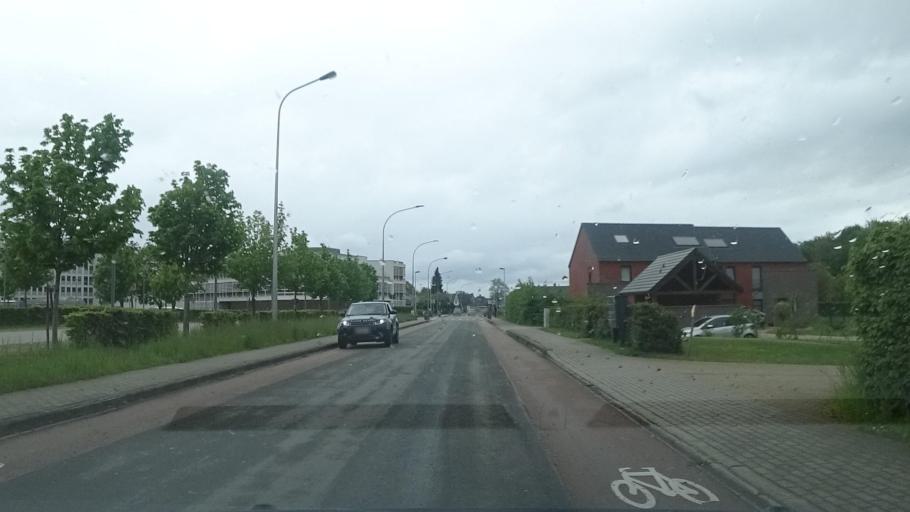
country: BE
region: Wallonia
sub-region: Province du Brabant Wallon
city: Ottignies
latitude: 50.6661
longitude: 4.5611
